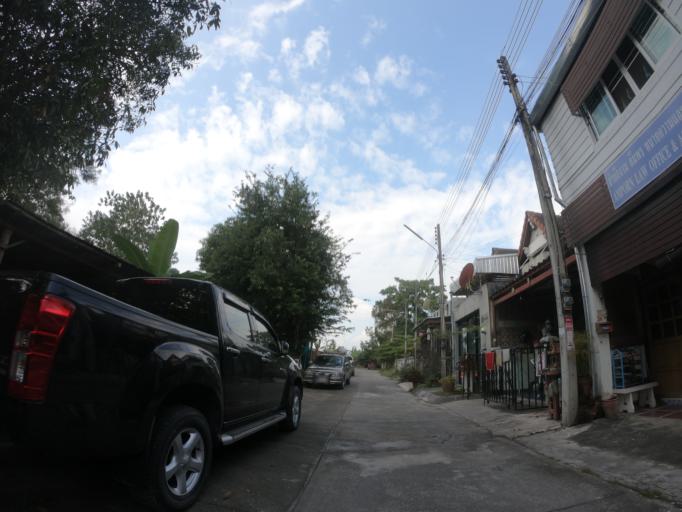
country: TH
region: Chiang Mai
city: Chiang Mai
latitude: 18.7568
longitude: 98.9671
